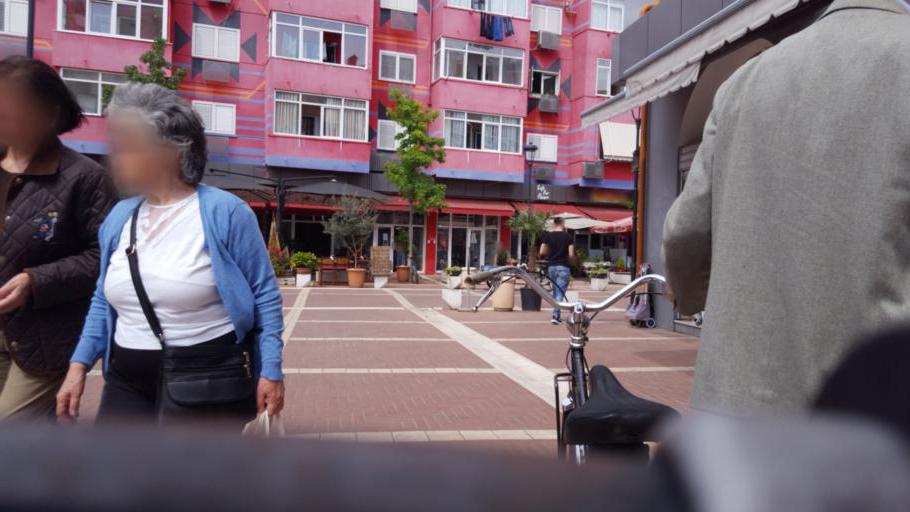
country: AL
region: Tirane
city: Tirana
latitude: 41.3305
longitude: 19.8244
